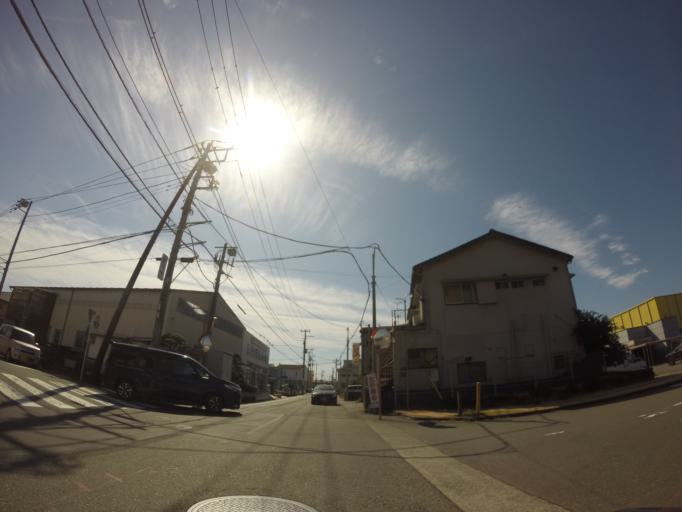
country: JP
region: Shizuoka
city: Numazu
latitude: 35.1188
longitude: 138.8210
